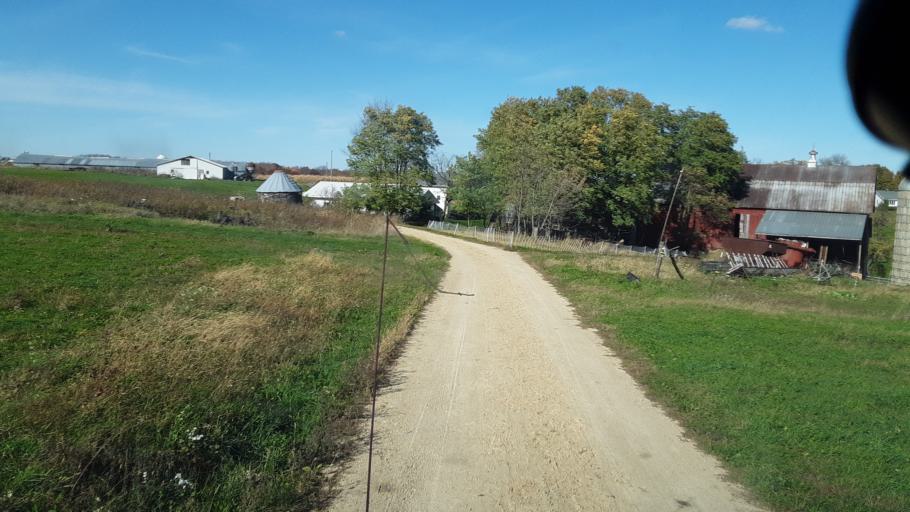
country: US
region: Wisconsin
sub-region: Vernon County
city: Hillsboro
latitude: 43.6849
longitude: -90.4094
